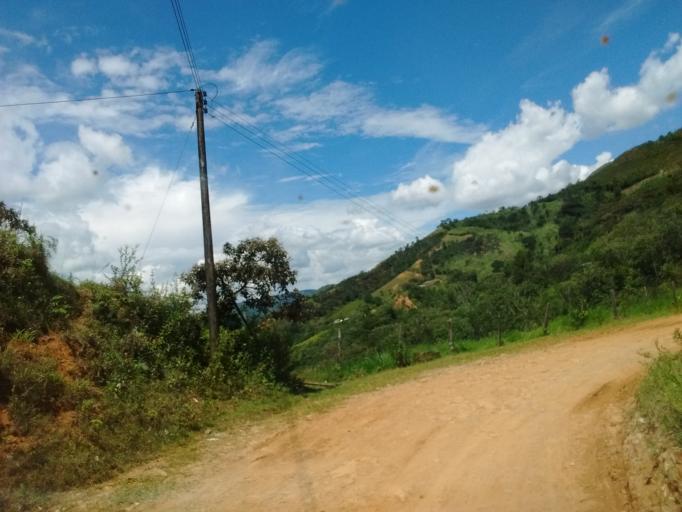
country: CO
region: Cauca
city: Villa Rica
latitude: 2.6389
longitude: -76.7693
